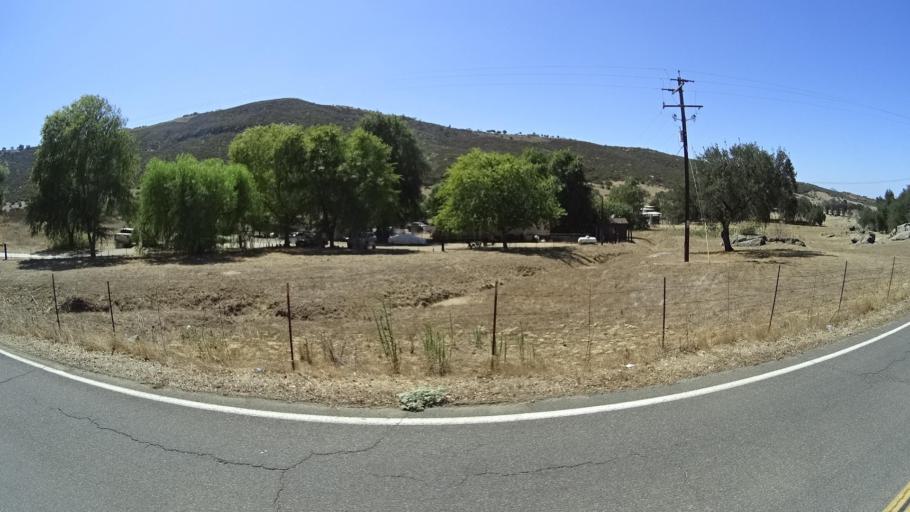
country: US
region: California
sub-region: San Diego County
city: San Diego Country Estates
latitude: 33.0508
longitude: -116.7957
